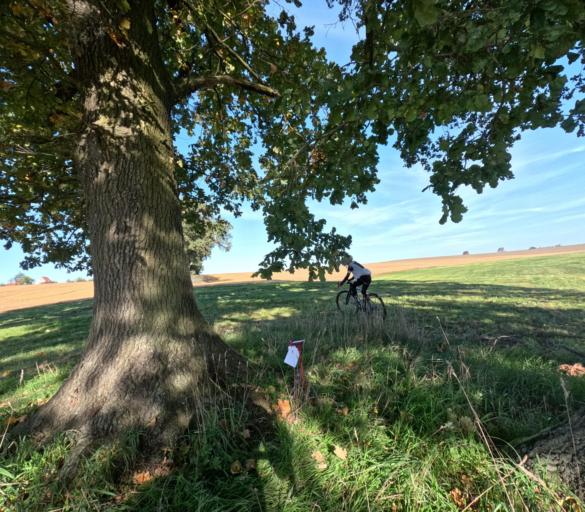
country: DE
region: Saxony
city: Ottendorf-Okrilla
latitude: 51.1436
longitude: 13.8257
